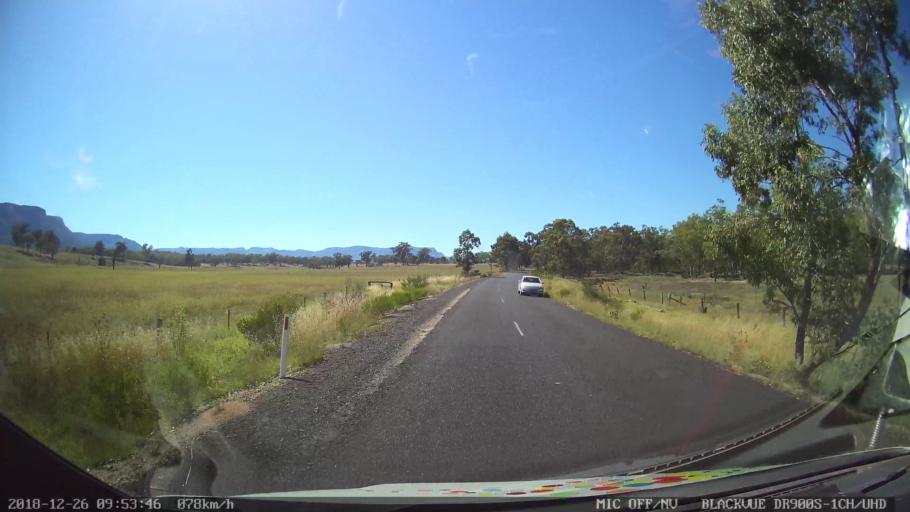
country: AU
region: New South Wales
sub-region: Mid-Western Regional
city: Kandos
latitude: -33.0241
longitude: 150.1557
